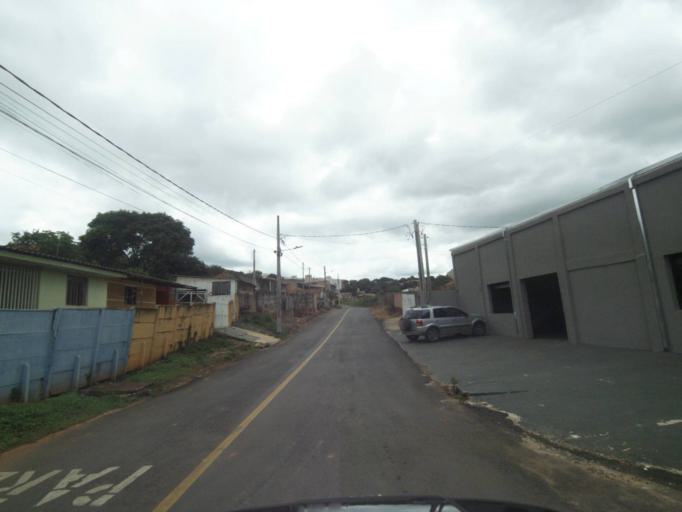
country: BR
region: Parana
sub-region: Telemaco Borba
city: Telemaco Borba
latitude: -24.3260
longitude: -50.6357
